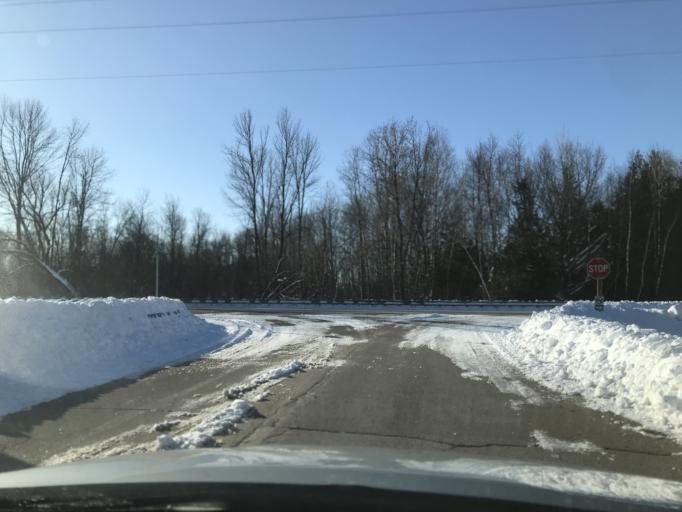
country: US
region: Wisconsin
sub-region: Oconto County
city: Oconto
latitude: 44.9505
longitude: -87.9771
